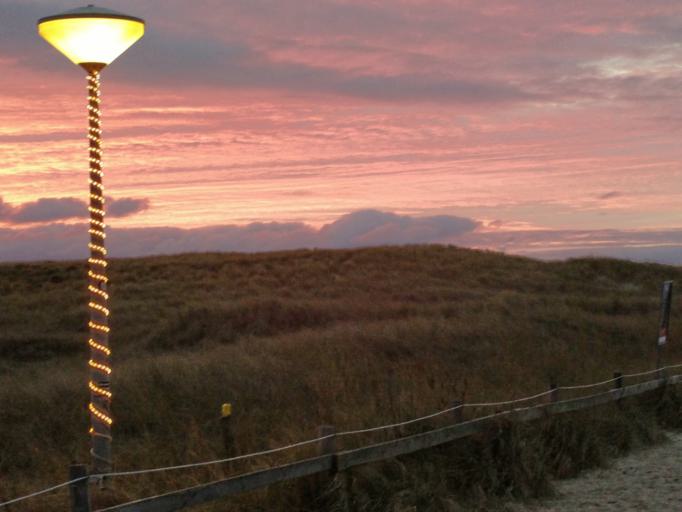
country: NL
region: North Holland
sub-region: Gemeente Texel
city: Den Burg
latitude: 53.0637
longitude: 4.7250
